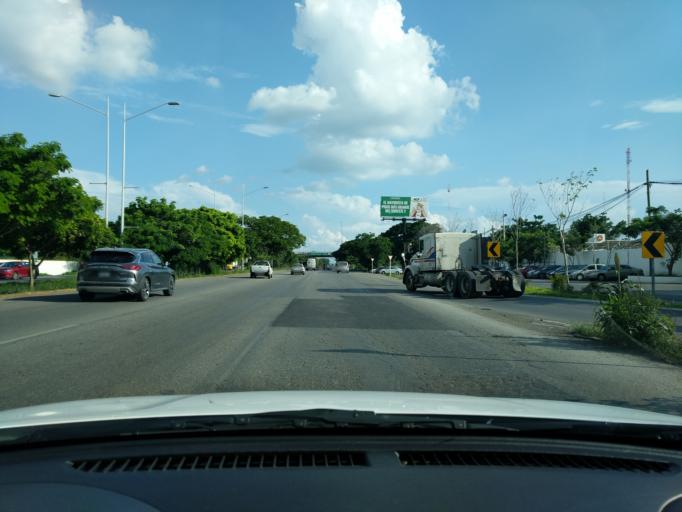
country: MX
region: Yucatan
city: Itzincab Palomeque
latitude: 20.9267
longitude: -89.6896
